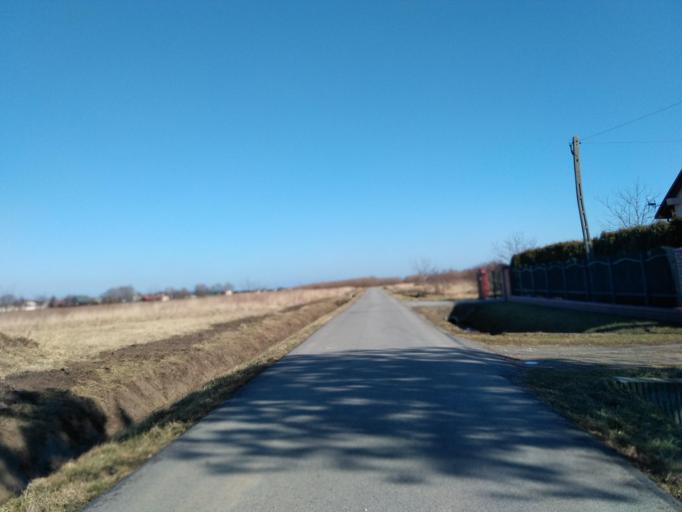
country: PL
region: Subcarpathian Voivodeship
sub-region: Powiat rzeszowski
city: Lutoryz
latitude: 49.9562
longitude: 21.9231
